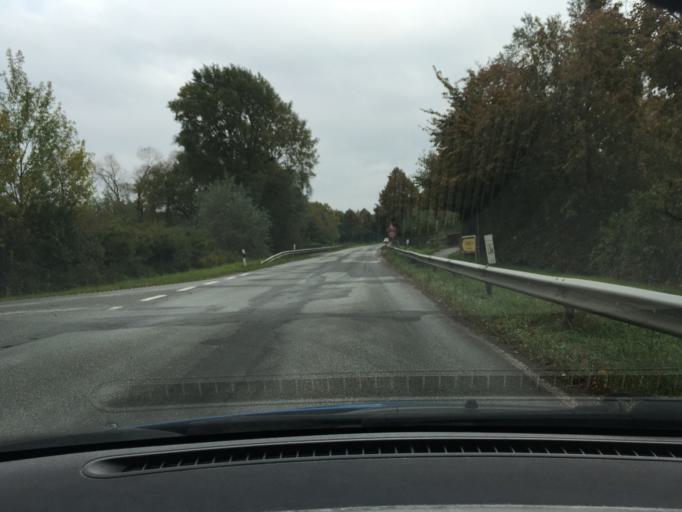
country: DE
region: Schleswig-Holstein
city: Klein Ronnau
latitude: 53.9673
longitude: 10.3179
